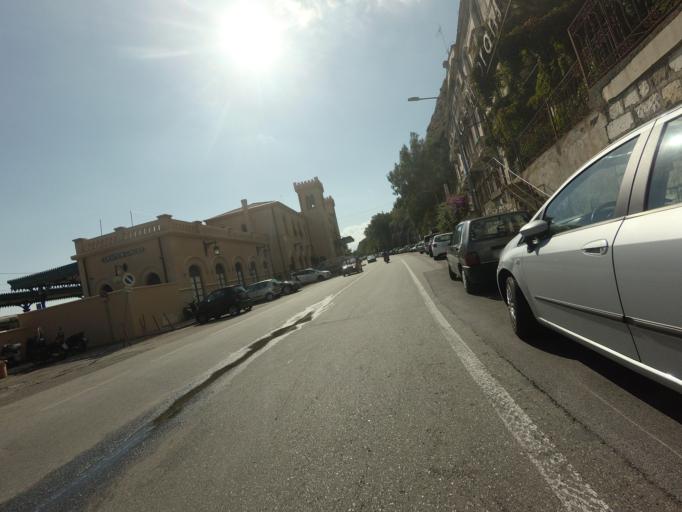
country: IT
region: Sicily
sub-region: Messina
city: Taormina
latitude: 37.8460
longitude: 15.2829
